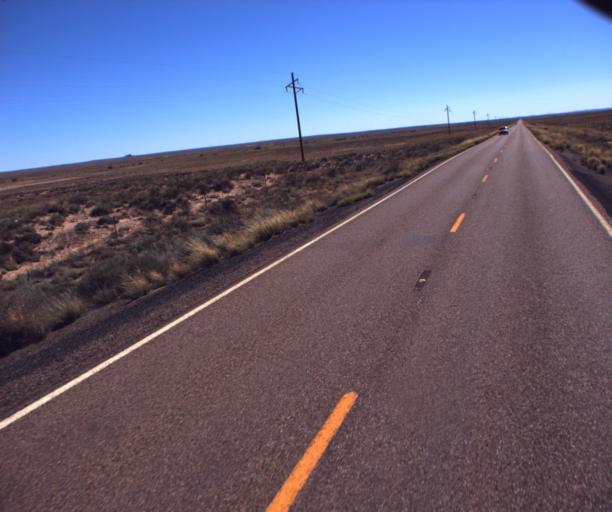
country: US
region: Arizona
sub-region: Navajo County
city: Holbrook
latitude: 35.1332
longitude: -110.0909
